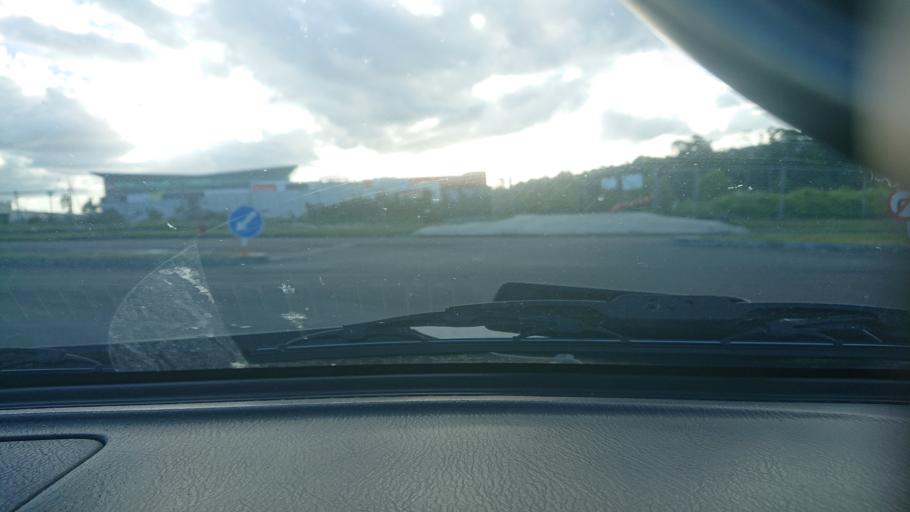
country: NZ
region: Auckland
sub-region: Auckland
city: Rothesay Bay
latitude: -36.7214
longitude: 174.7089
